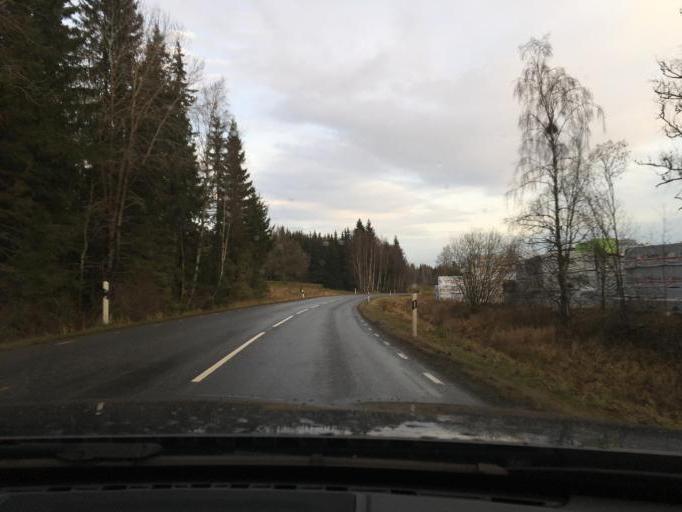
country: SE
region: Joenkoeping
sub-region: Jonkopings Kommun
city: Kaxholmen
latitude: 57.9166
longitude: 14.3897
